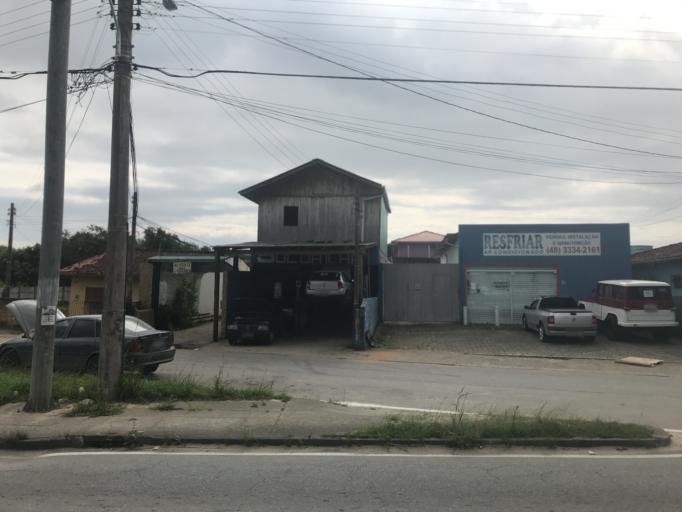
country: BR
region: Santa Catarina
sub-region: Florianopolis
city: Costeira do Pirajubae
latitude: -27.6483
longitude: -48.5216
